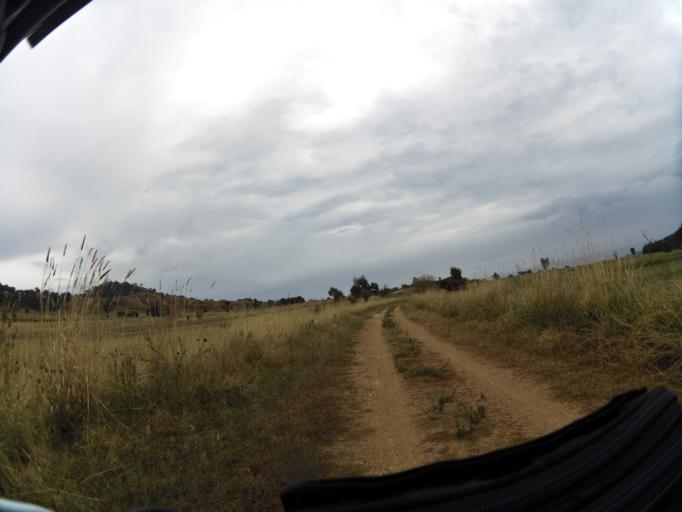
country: AU
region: New South Wales
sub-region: Albury Municipality
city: East Albury
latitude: -36.2161
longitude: 147.0582
